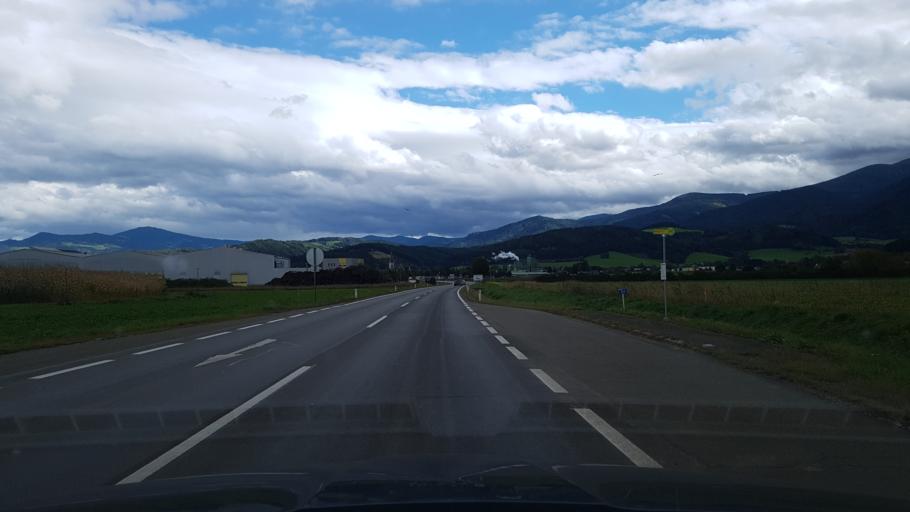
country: AT
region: Styria
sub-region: Politischer Bezirk Murtal
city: Weisskirchen in Steiermark
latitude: 47.1582
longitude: 14.7191
